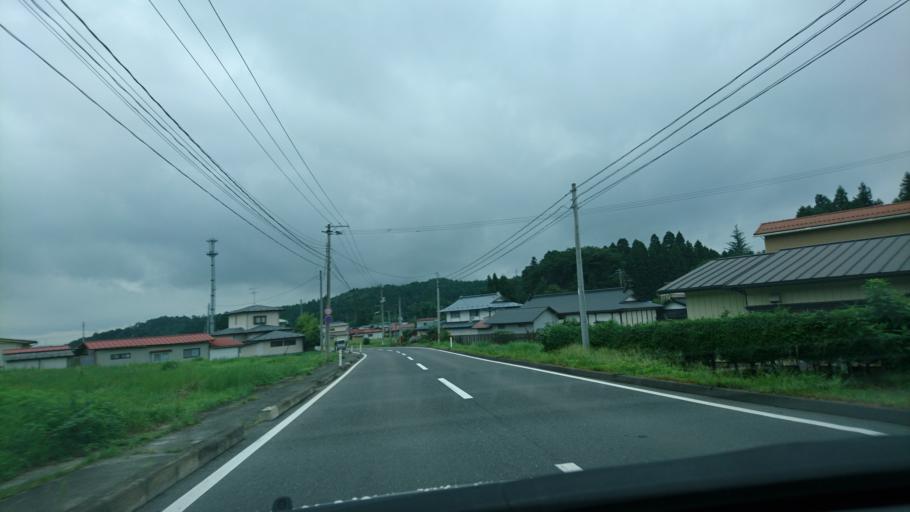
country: JP
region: Iwate
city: Ichinoseki
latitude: 38.8053
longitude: 140.9343
